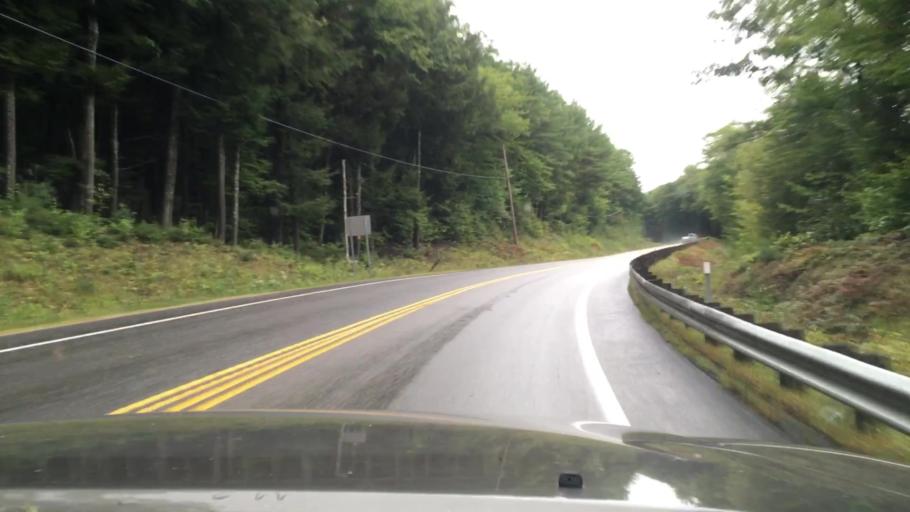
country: US
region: New Hampshire
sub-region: Hillsborough County
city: Antrim
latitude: 43.0754
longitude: -71.9844
